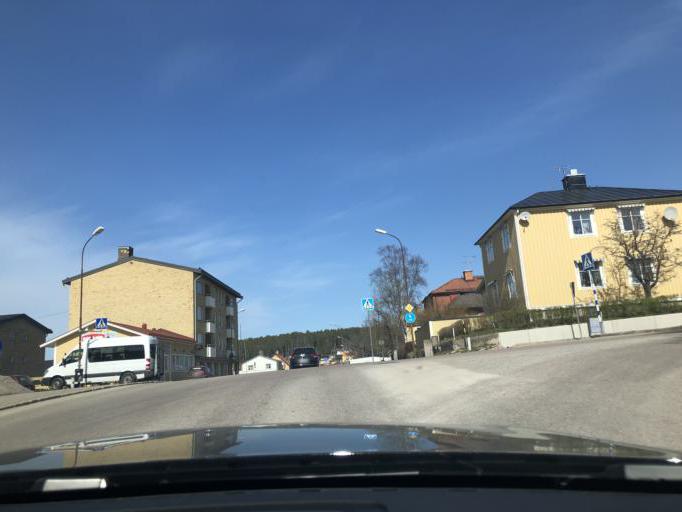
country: SE
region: Gaevleborg
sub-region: Hudiksvalls Kommun
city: Hudiksvall
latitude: 61.7279
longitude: 17.1225
